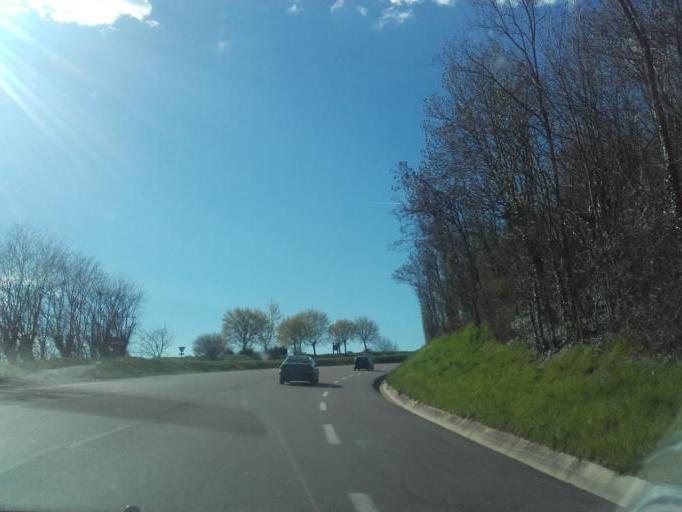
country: FR
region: Rhone-Alpes
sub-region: Departement de l'Isere
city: Saint-Hilaire-de-la-Cote
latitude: 45.3995
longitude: 5.3507
